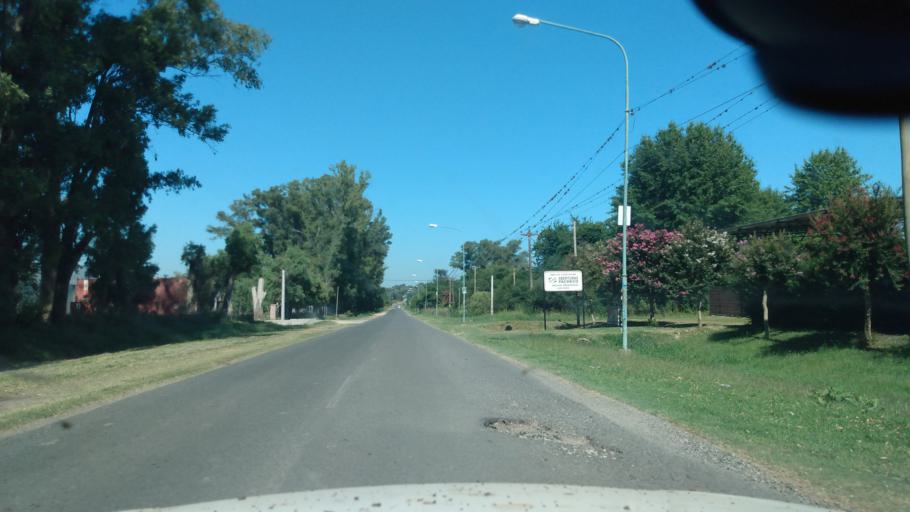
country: AR
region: Buenos Aires
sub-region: Partido de Lujan
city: Lujan
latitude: -34.5059
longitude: -59.0790
